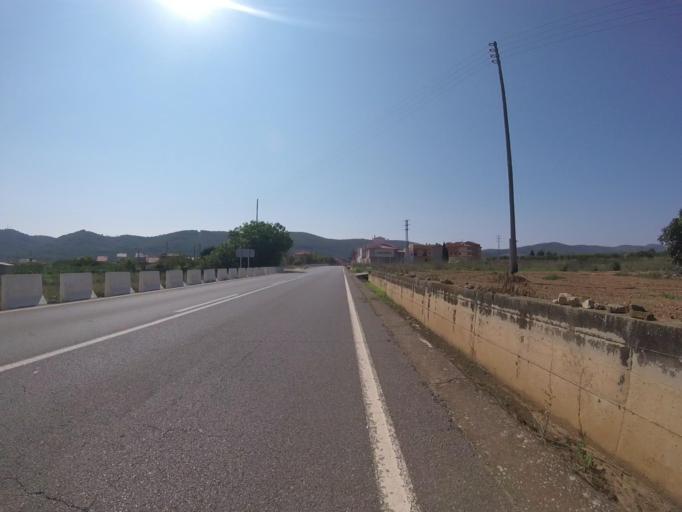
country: ES
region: Valencia
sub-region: Provincia de Castello
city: Adzaneta
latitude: 40.2221
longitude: -0.1722
